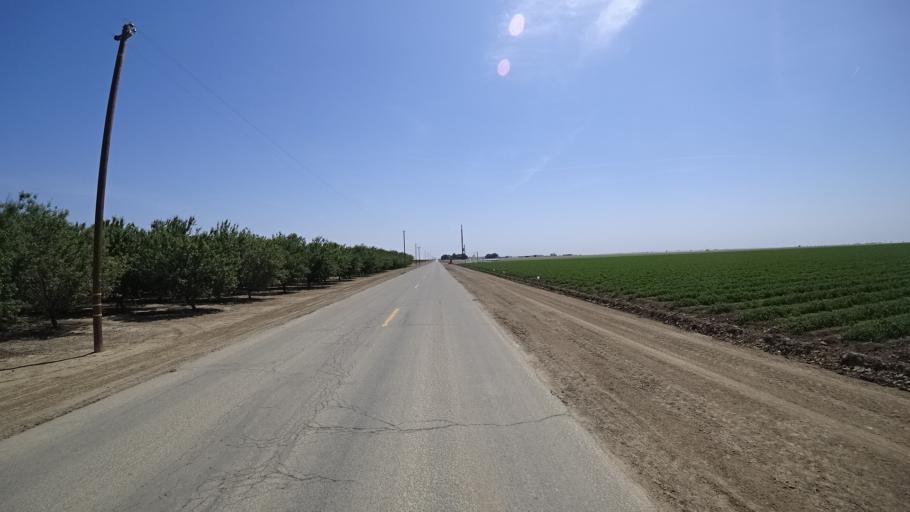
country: US
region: California
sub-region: Fresno County
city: Huron
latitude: 36.1377
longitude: -119.9972
